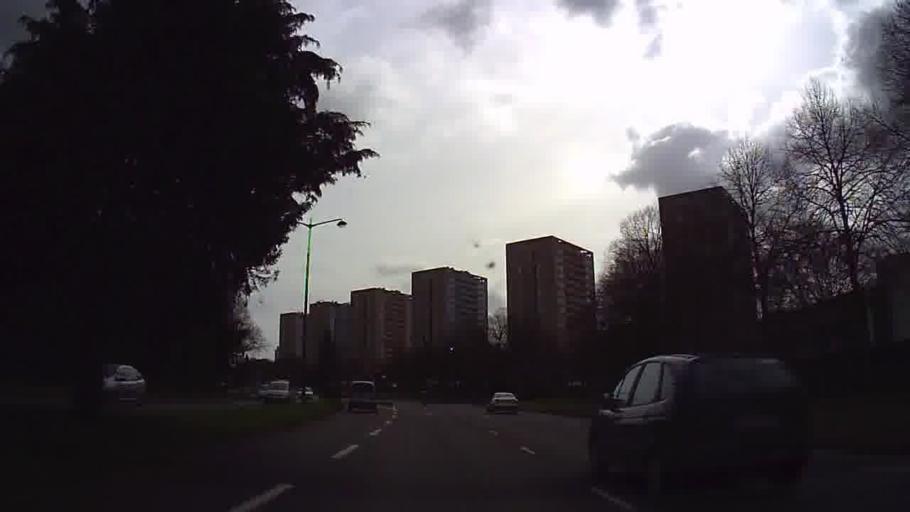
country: FR
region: Brittany
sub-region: Departement d'Ille-et-Vilaine
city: Rennes
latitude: 48.1289
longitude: -1.6655
